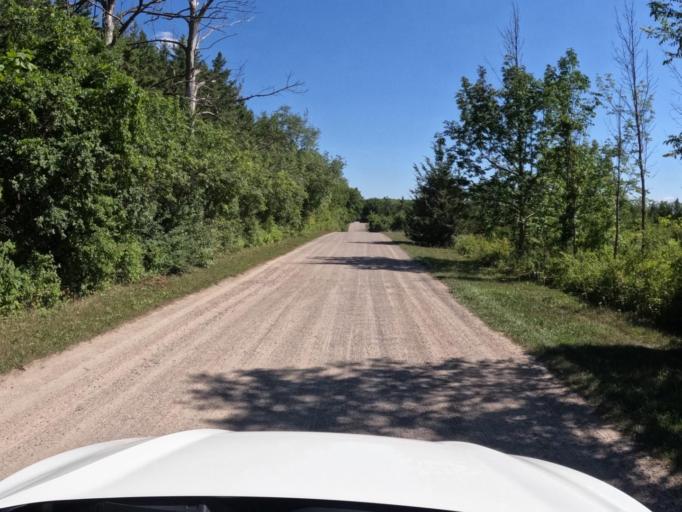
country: CA
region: Ontario
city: Cambridge
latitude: 43.4237
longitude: -80.2541
